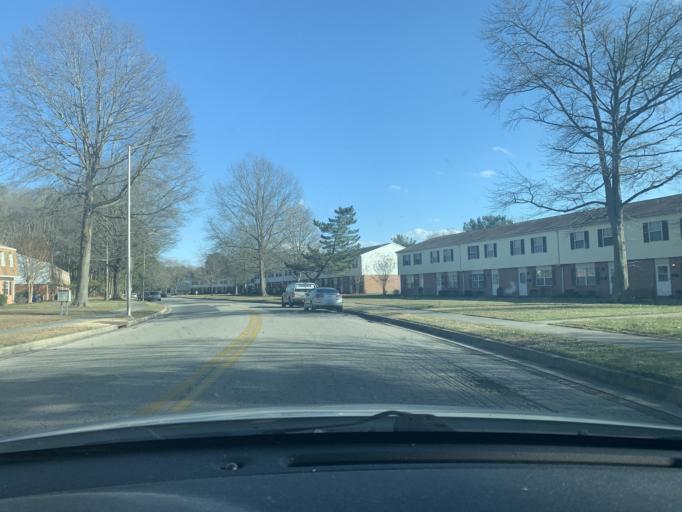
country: US
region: Maryland
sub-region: Wicomico County
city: Salisbury
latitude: 38.3816
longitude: -75.5746
